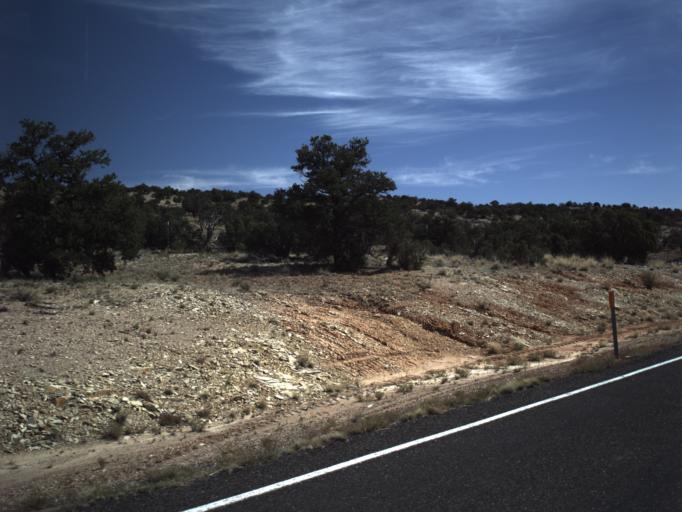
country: US
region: Utah
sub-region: Wayne County
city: Loa
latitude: 37.7379
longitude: -111.5477
